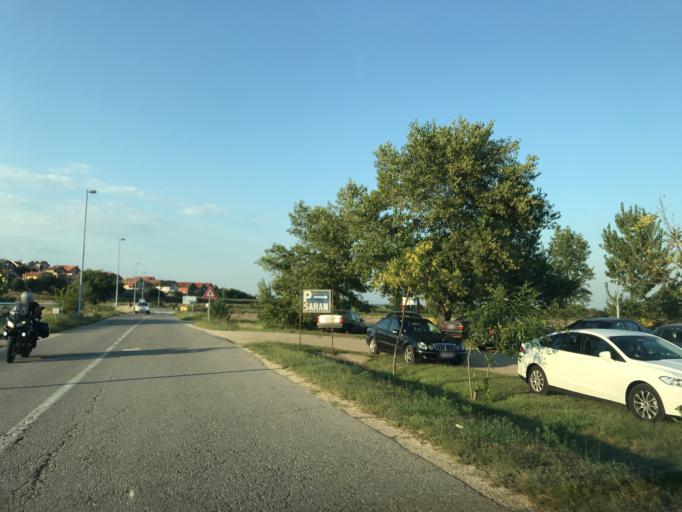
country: RO
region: Mehedinti
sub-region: Comuna Gogosu
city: Ostrovu Mare
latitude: 44.4843
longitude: 22.4565
